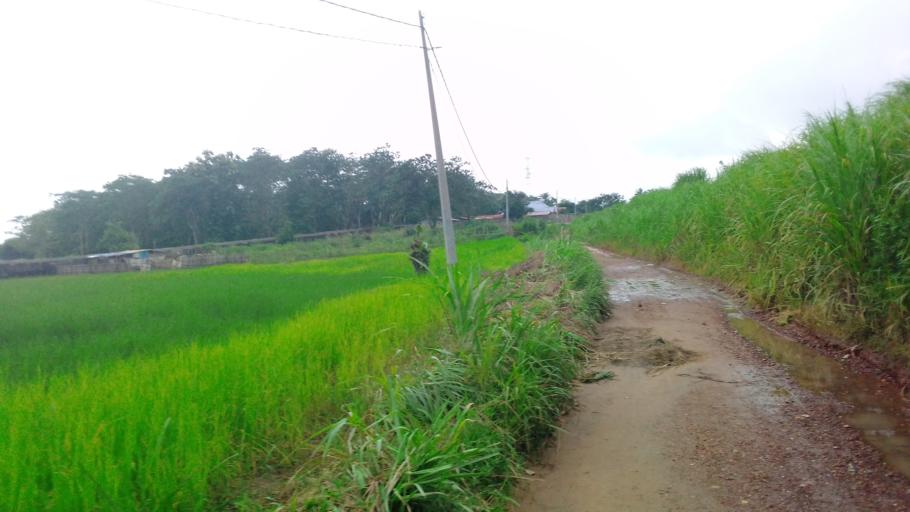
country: SL
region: Northern Province
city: Lunsar
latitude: 8.6915
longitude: -12.5482
